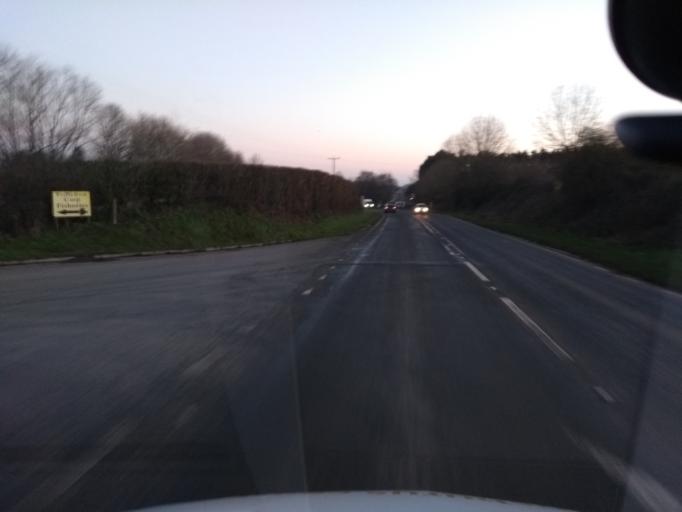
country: GB
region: England
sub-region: Somerset
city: North Petherton
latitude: 51.0807
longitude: -3.0175
